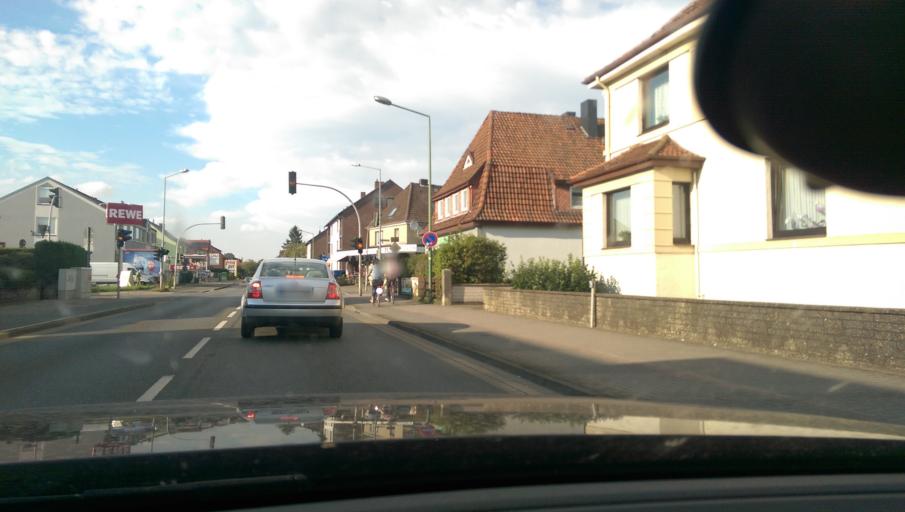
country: DE
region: Lower Saxony
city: Neustadt am Rubenberge
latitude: 52.4993
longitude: 9.4569
